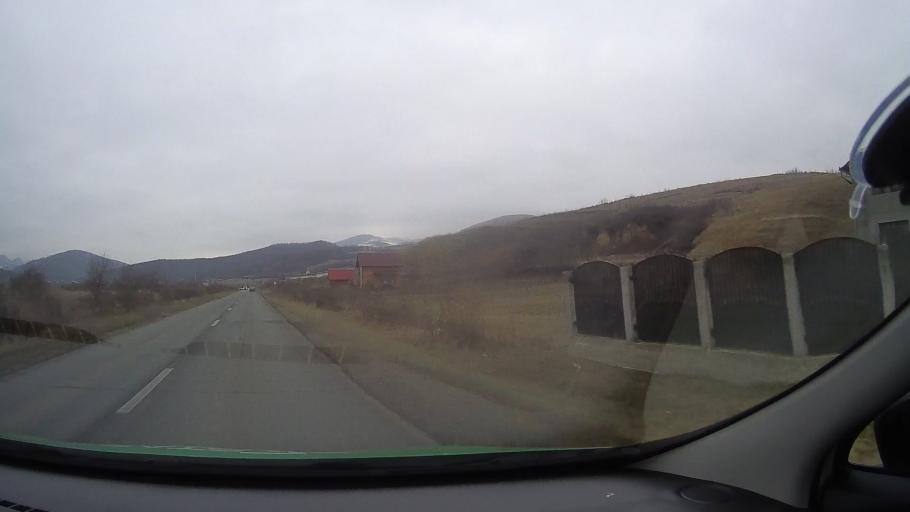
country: RO
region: Alba
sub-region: Comuna Ighiu
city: Sard
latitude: 46.1202
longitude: 23.5069
